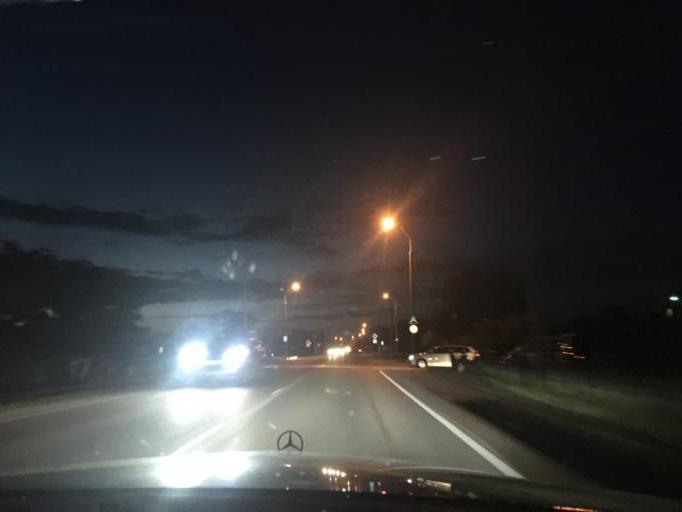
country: BY
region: Brest
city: Brest
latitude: 52.0644
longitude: 23.6880
